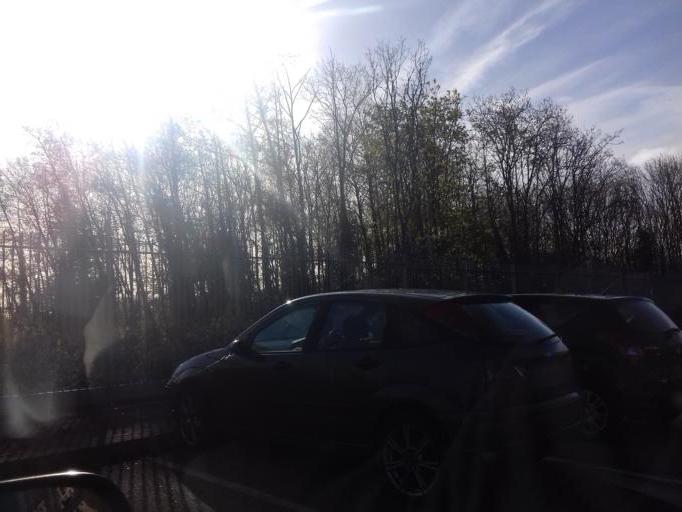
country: IE
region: Leinster
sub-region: Dublin City
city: Finglas
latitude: 53.3989
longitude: -6.2871
